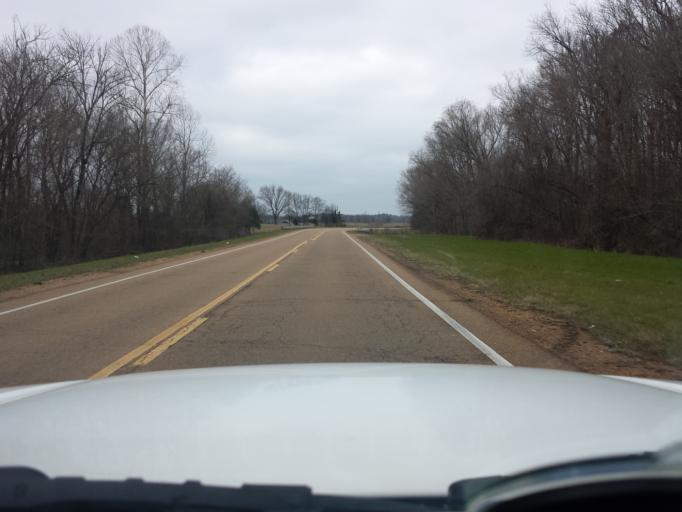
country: US
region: Mississippi
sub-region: Madison County
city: Canton
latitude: 32.7550
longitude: -90.1497
